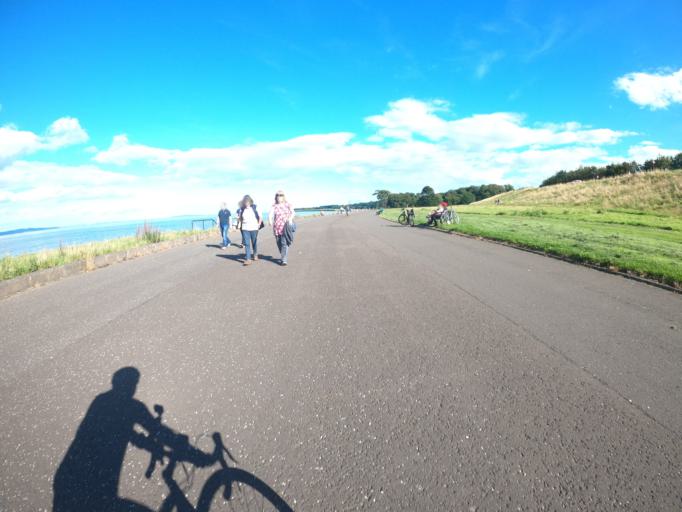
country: GB
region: Scotland
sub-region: Fife
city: Aberdour
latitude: 55.9800
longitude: -3.2765
